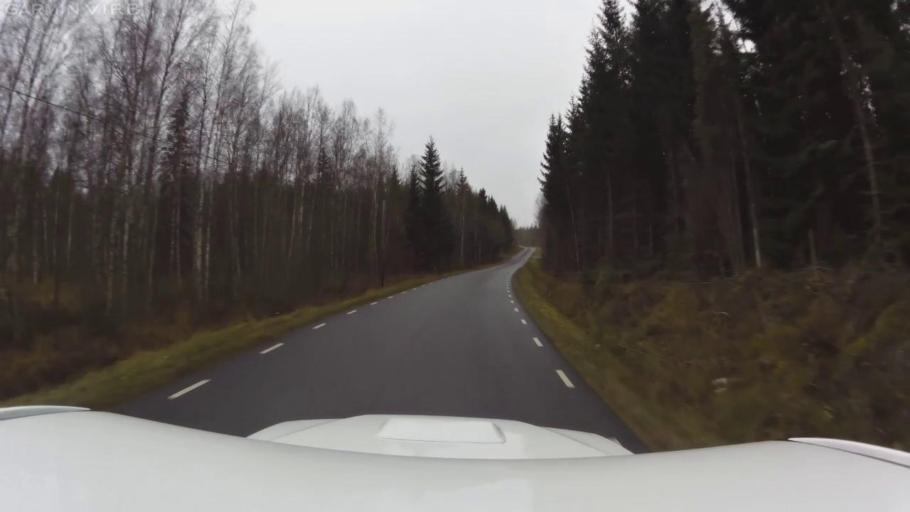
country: SE
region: OEstergoetland
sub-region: Mjolby Kommun
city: Mantorp
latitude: 58.1504
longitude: 15.3930
